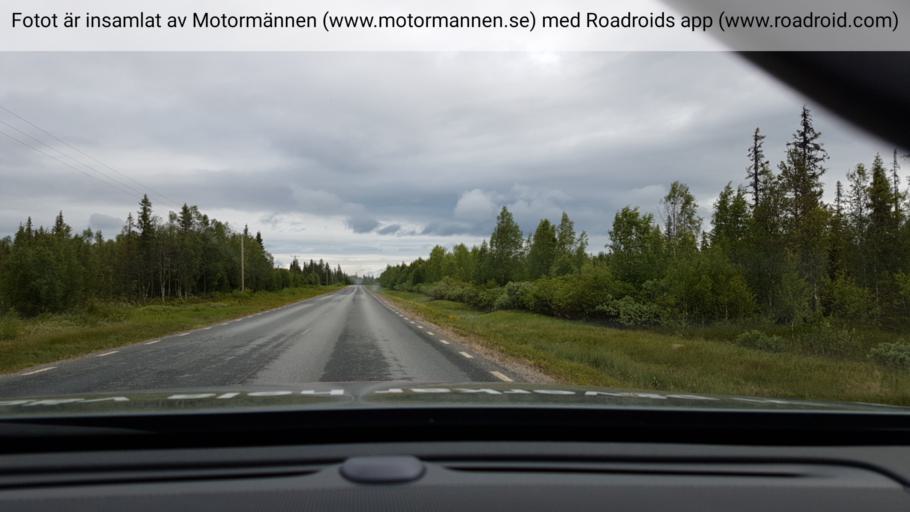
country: SE
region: Vaesterbotten
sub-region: Lycksele Kommun
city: Soderfors
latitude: 64.4146
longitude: 18.0278
